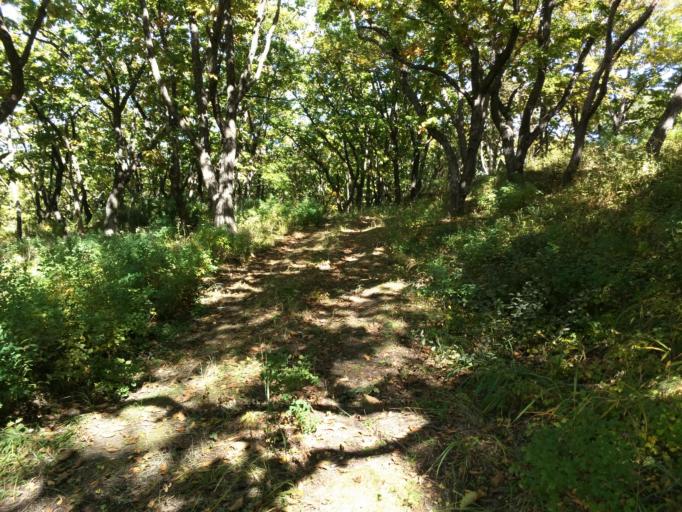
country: RU
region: Primorskiy
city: Zarubino
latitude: 42.6906
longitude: 131.2389
